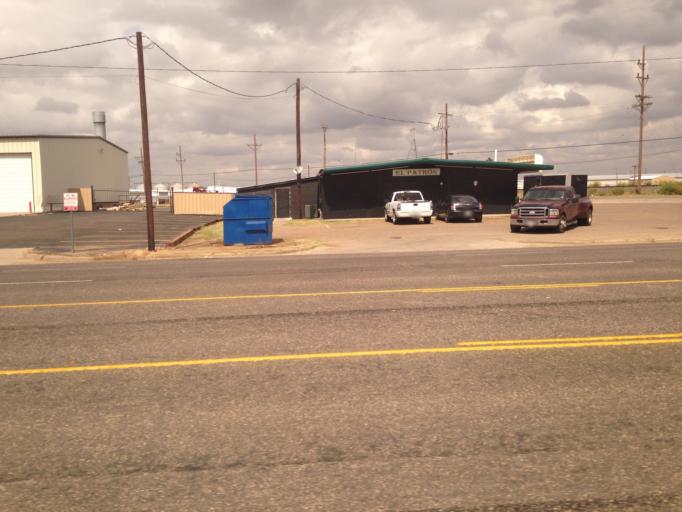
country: US
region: Texas
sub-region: Lubbock County
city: Lubbock
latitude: 33.5489
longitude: -101.8051
